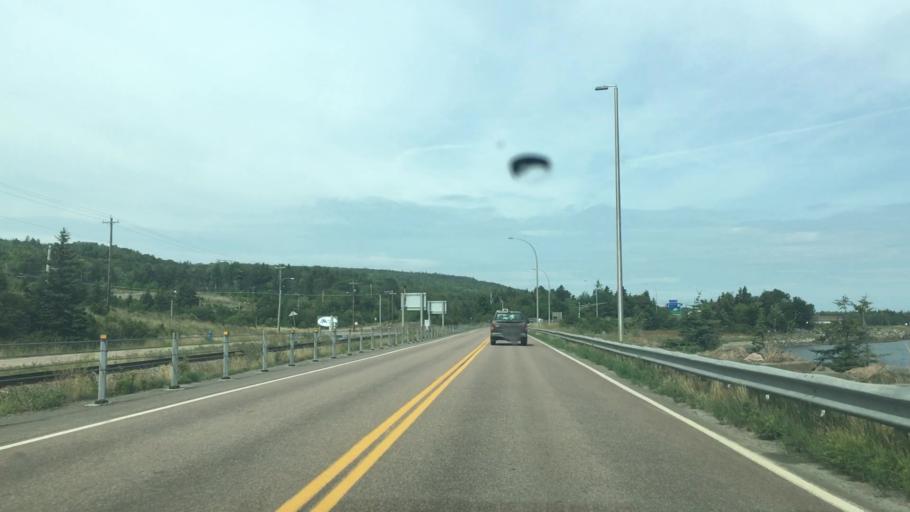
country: CA
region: Nova Scotia
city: Port Hawkesbury
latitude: 45.6442
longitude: -61.4330
